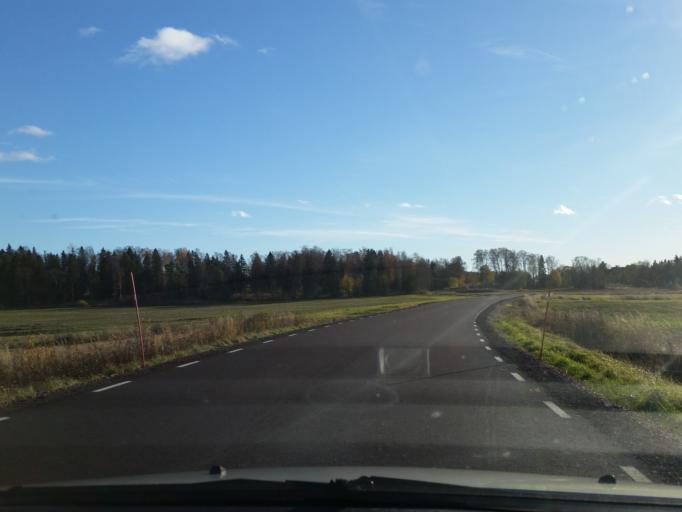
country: AX
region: Alands landsbygd
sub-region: Jomala
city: Jomala
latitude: 60.1937
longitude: 19.9597
